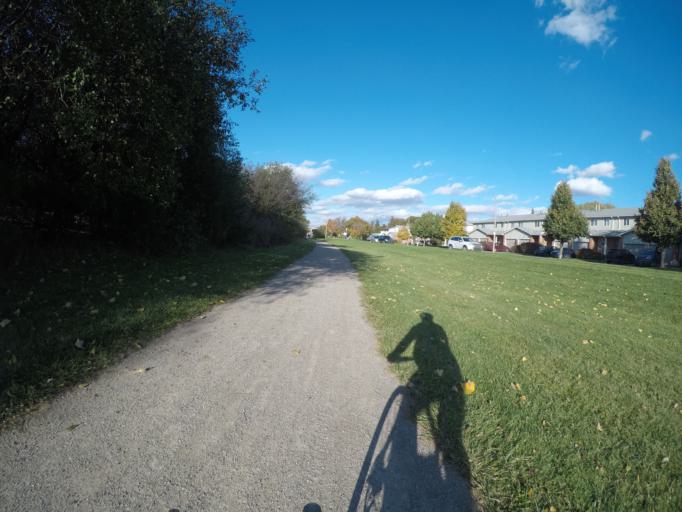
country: CA
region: Ontario
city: Kitchener
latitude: 43.4330
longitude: -80.4579
